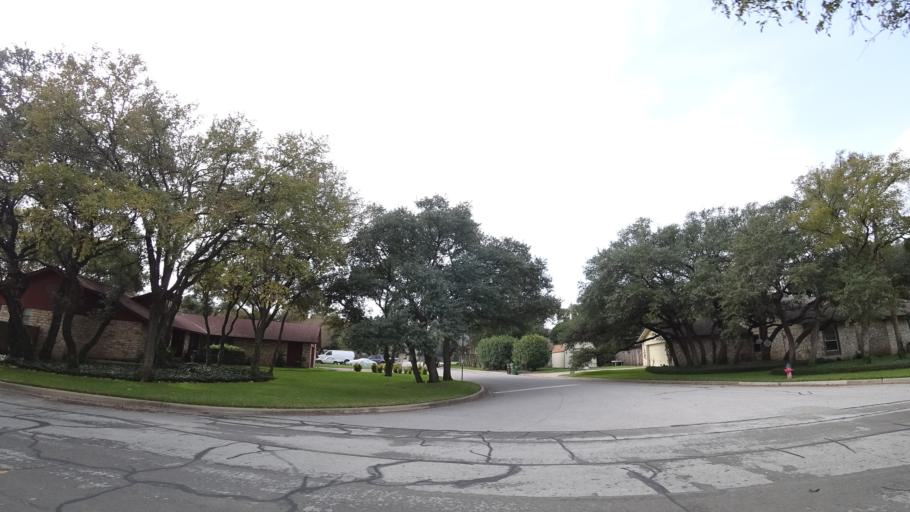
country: US
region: Texas
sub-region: Williamson County
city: Round Rock
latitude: 30.4960
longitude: -97.6903
